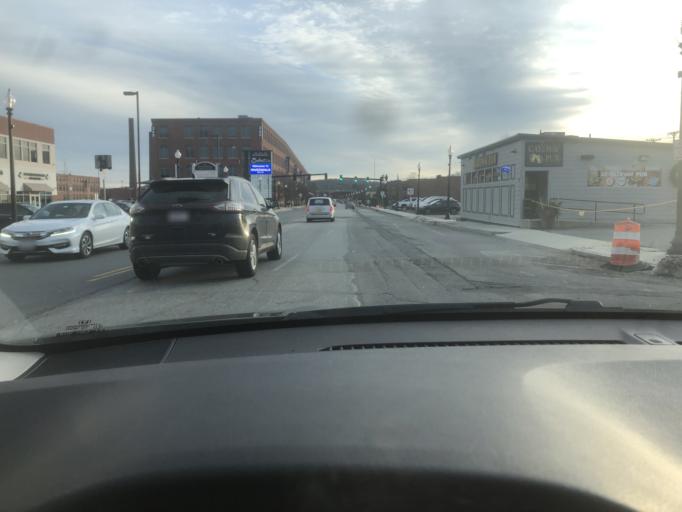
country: US
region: Massachusetts
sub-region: Essex County
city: North Andover
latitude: 42.7029
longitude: -71.1472
